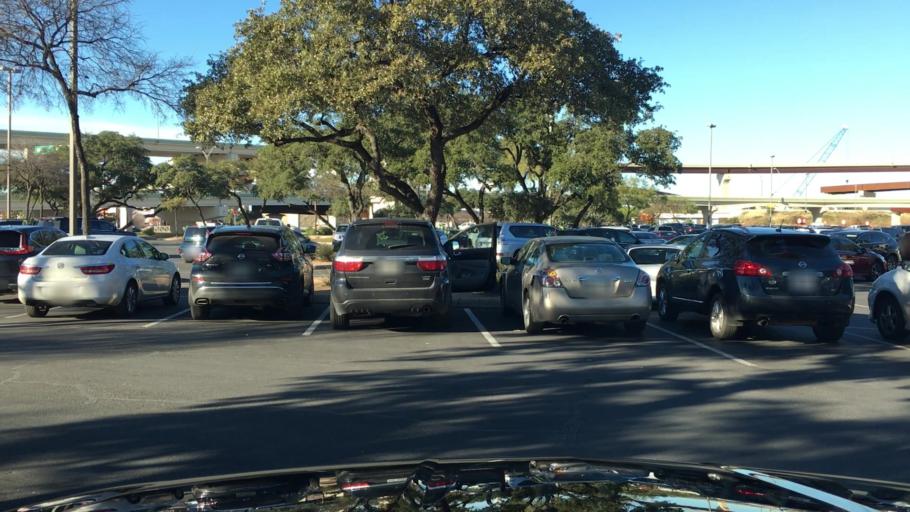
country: US
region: Texas
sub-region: Bexar County
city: Hollywood Park
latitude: 29.6057
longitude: -98.4679
